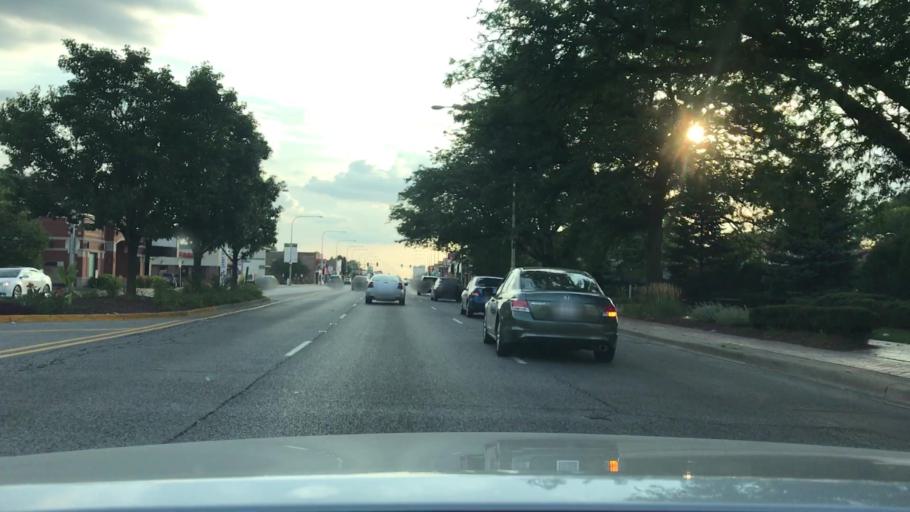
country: US
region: Illinois
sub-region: Cook County
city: Evergreen Park
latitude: 41.7208
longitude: -87.7031
